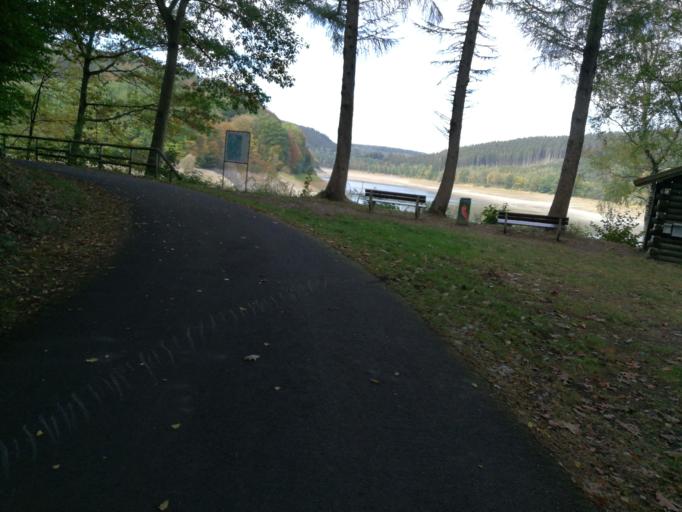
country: DE
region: North Rhine-Westphalia
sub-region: Regierungsbezirk Arnsberg
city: Meschede
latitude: 51.3141
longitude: 8.2726
